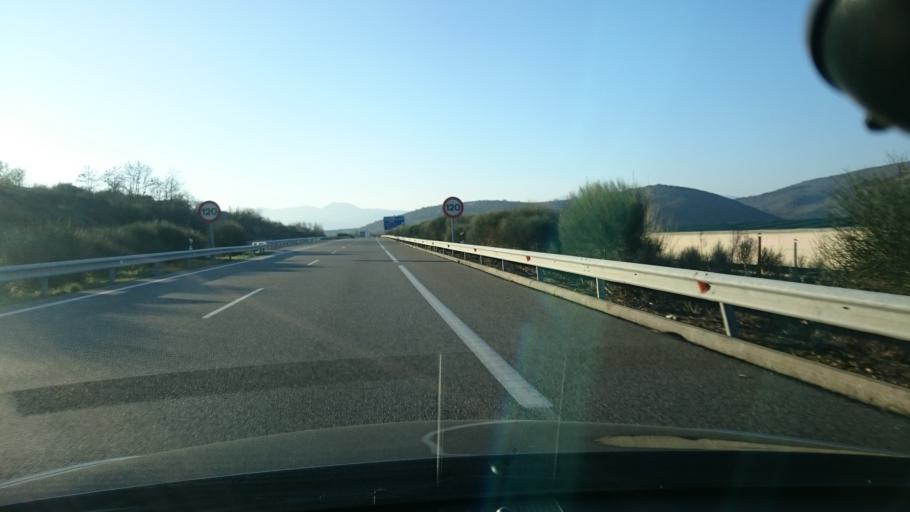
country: ES
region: Castille and Leon
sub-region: Provincia de Leon
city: Villafranca del Bierzo
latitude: 42.5926
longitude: -6.7963
